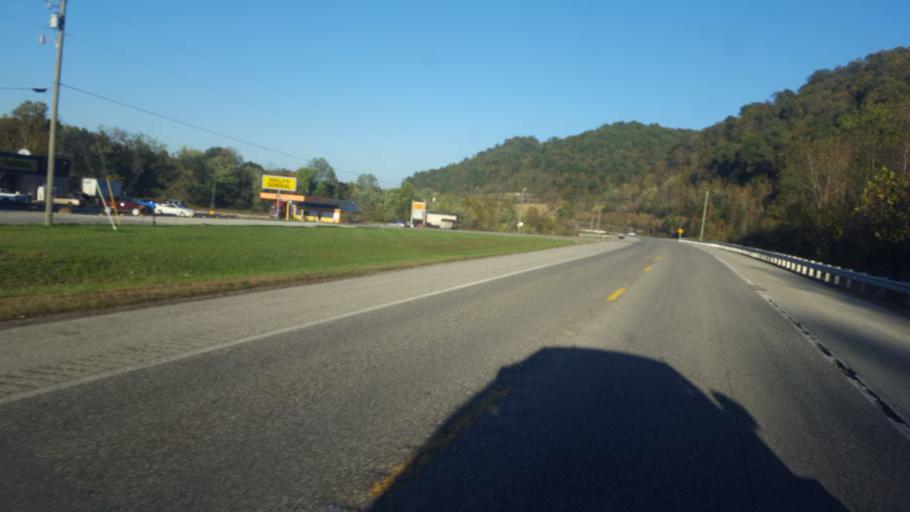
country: US
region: Kentucky
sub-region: Lewis County
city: Vanceburg
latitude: 38.5945
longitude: -83.1816
